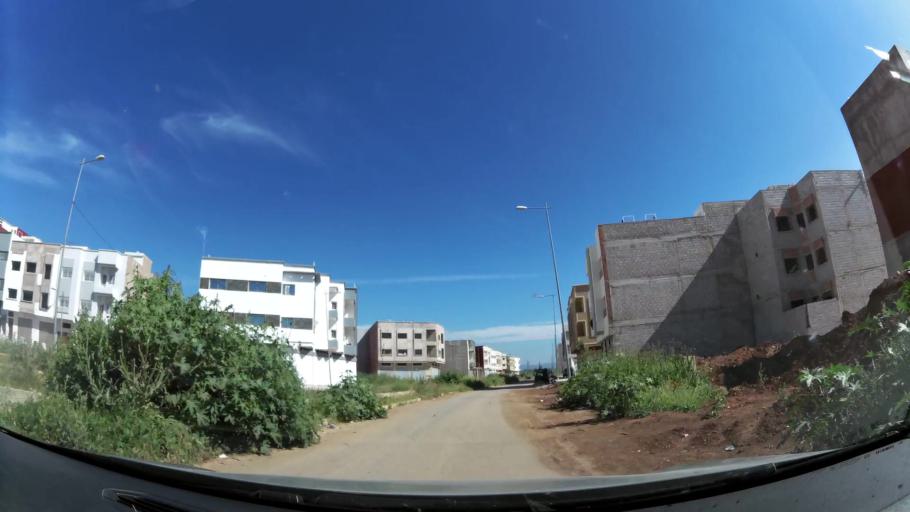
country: MA
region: Fes-Boulemane
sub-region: Fes
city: Fes
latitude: 33.9938
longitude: -5.0070
